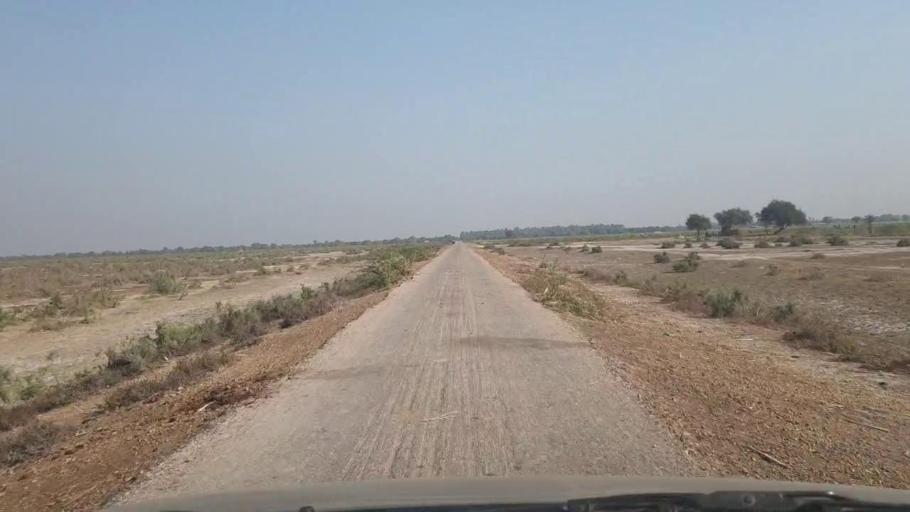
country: PK
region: Sindh
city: Digri
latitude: 25.2649
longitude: 69.1681
